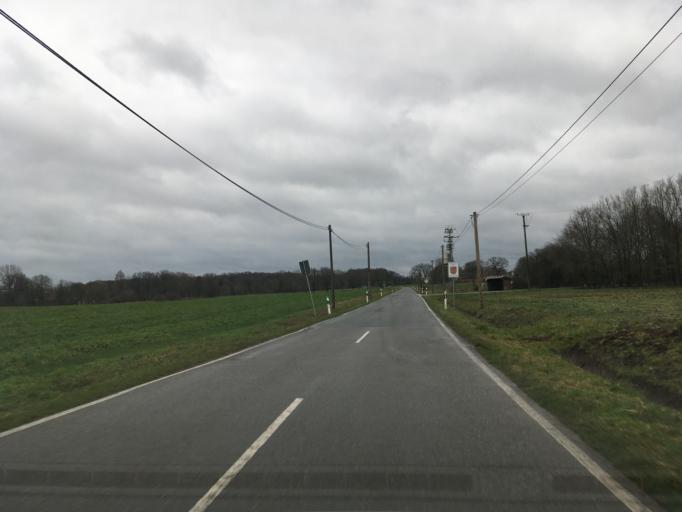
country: DE
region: North Rhine-Westphalia
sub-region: Regierungsbezirk Munster
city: Legden
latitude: 52.0452
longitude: 7.1667
